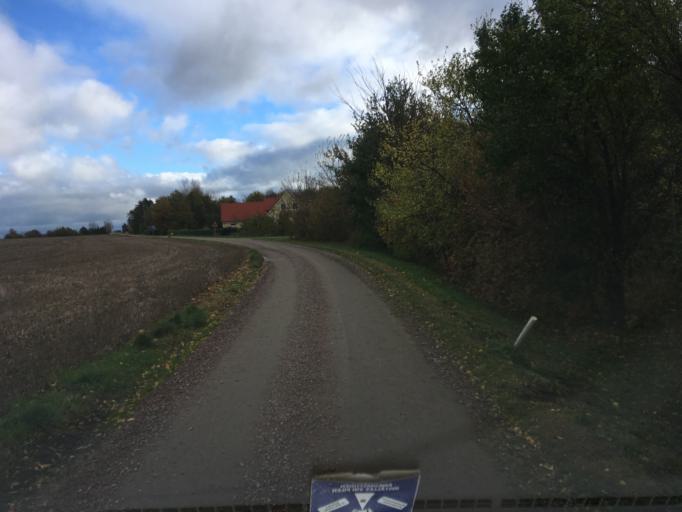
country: SE
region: Skane
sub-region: Lunds Kommun
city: Lund
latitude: 55.7396
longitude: 13.2089
